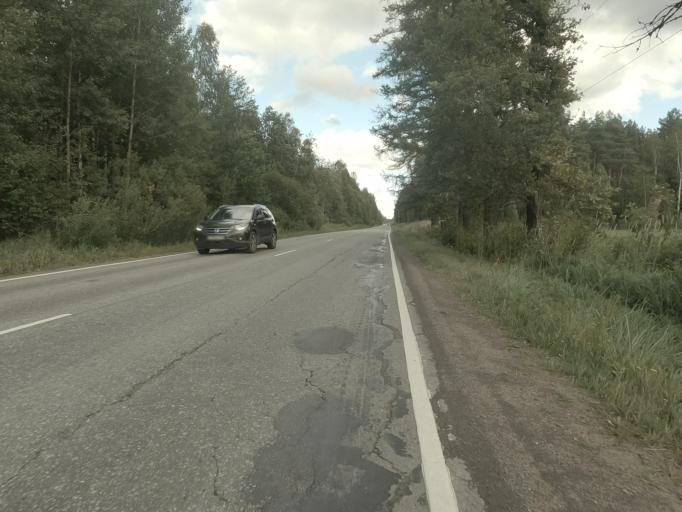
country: RU
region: Leningrad
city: Shcheglovo
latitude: 60.0284
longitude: 30.8003
